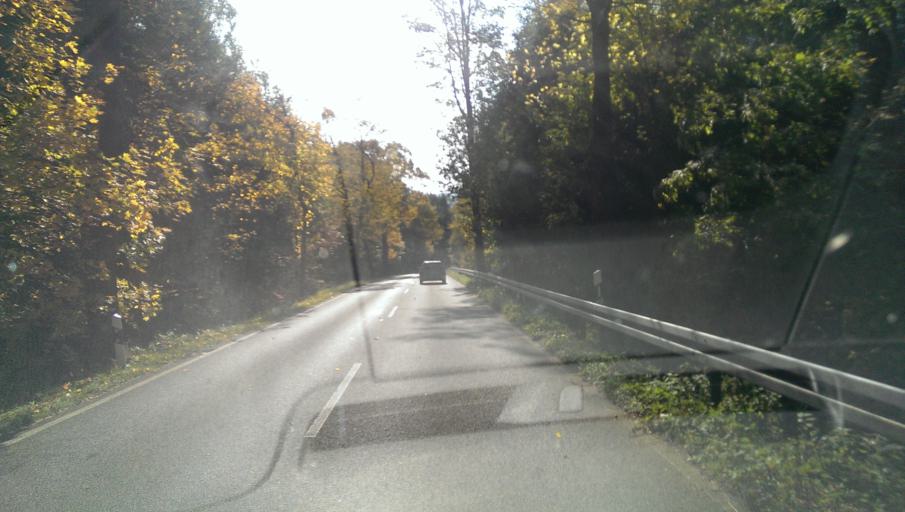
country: DE
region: Saxony
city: Dohma
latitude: 50.8390
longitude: 13.9653
